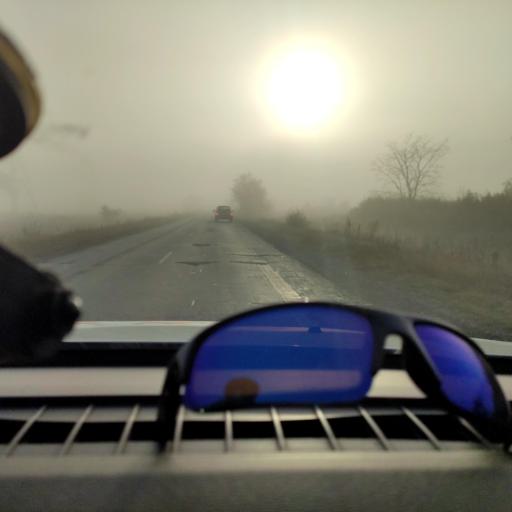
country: RU
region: Samara
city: Chapayevsk
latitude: 53.0005
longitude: 49.7627
